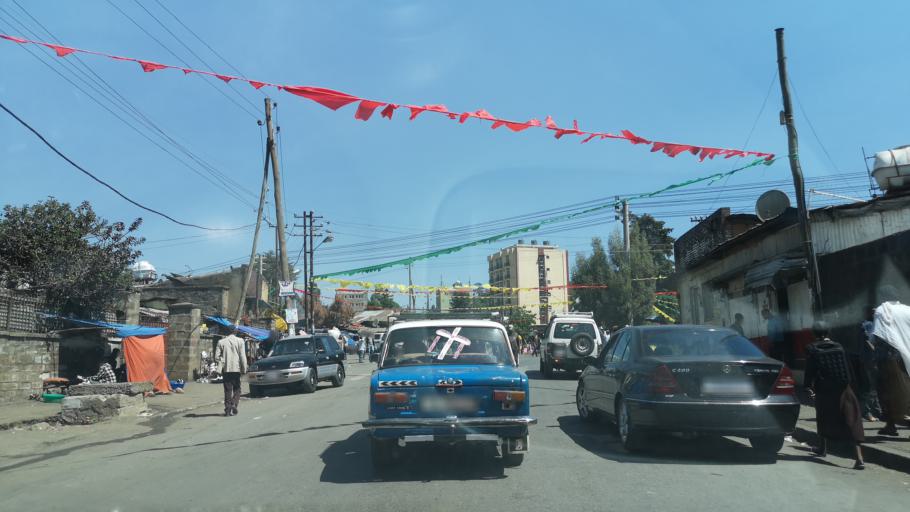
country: ET
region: Adis Abeba
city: Addis Ababa
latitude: 9.0520
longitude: 38.7496
